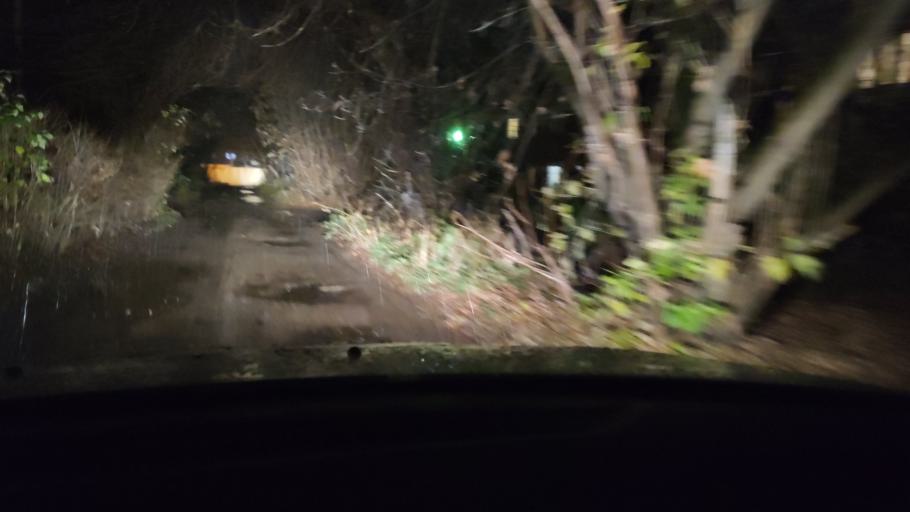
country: RU
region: Perm
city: Perm
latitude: 57.9600
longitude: 56.2300
